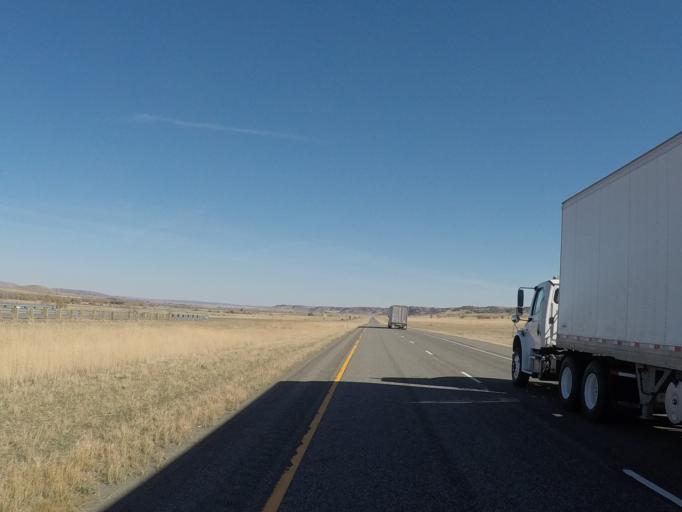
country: US
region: Montana
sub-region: Sweet Grass County
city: Big Timber
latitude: 45.7511
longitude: -110.1576
